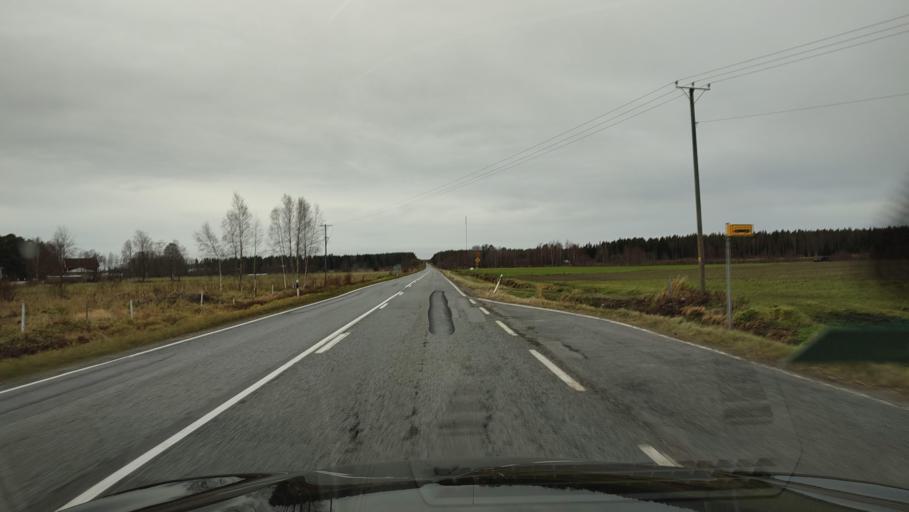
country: FI
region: Ostrobothnia
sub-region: Sydosterbotten
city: Naerpes
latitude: 62.4050
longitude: 21.3902
